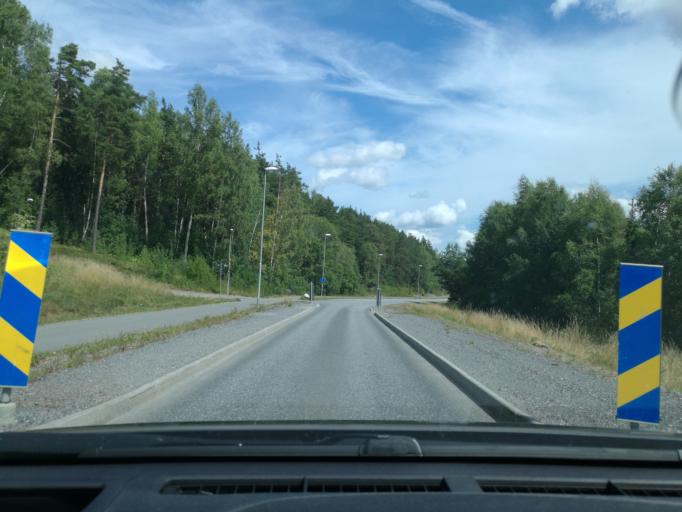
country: SE
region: Stockholm
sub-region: Sigtuna Kommun
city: Marsta
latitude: 59.6119
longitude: 17.8361
